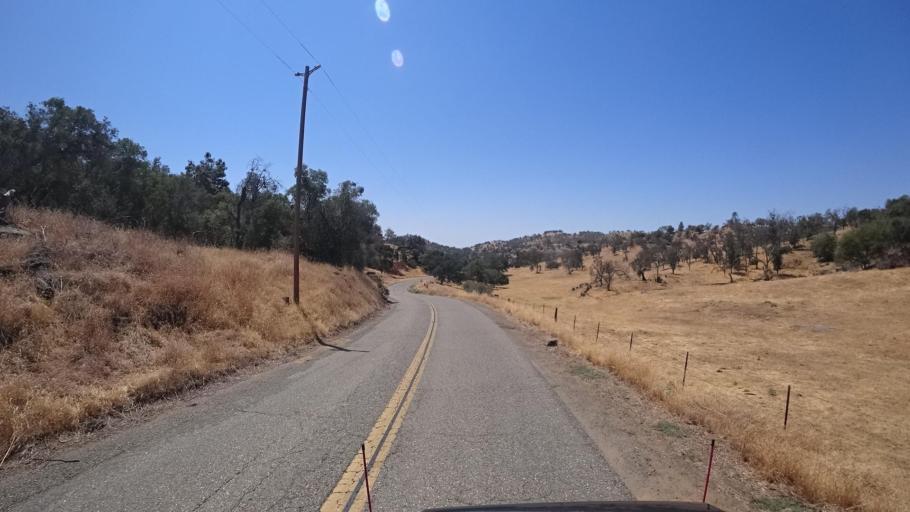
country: US
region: California
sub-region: Mariposa County
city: Mariposa
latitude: 37.2906
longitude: -119.9774
